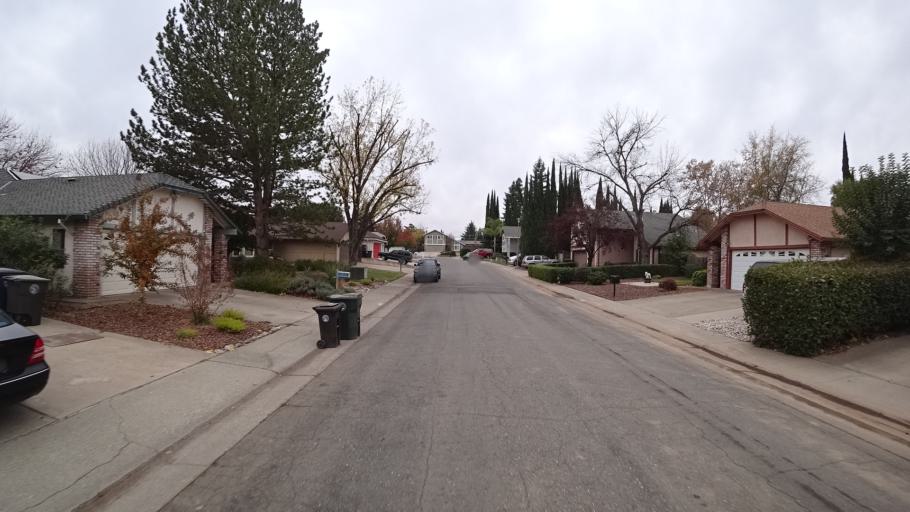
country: US
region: California
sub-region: Sacramento County
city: Citrus Heights
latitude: 38.7030
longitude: -121.2918
